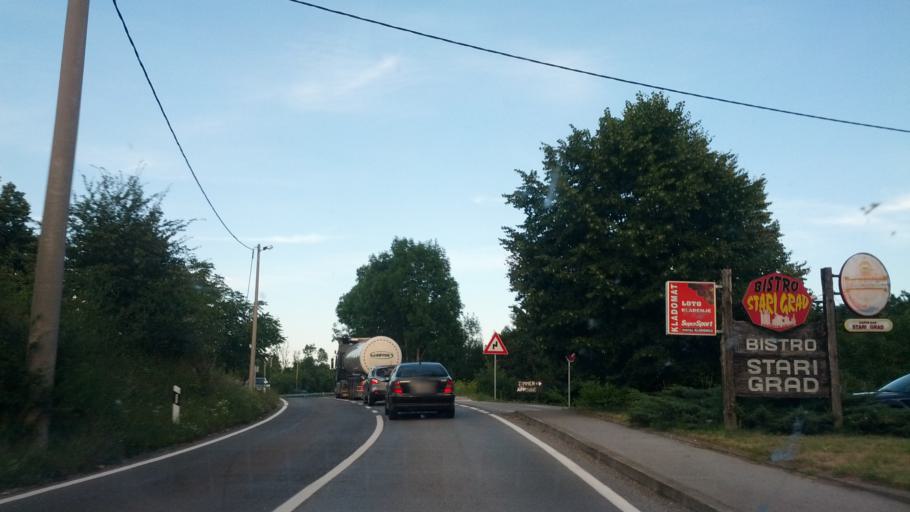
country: HR
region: Licko-Senjska
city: Jezerce
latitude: 44.9569
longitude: 15.6623
